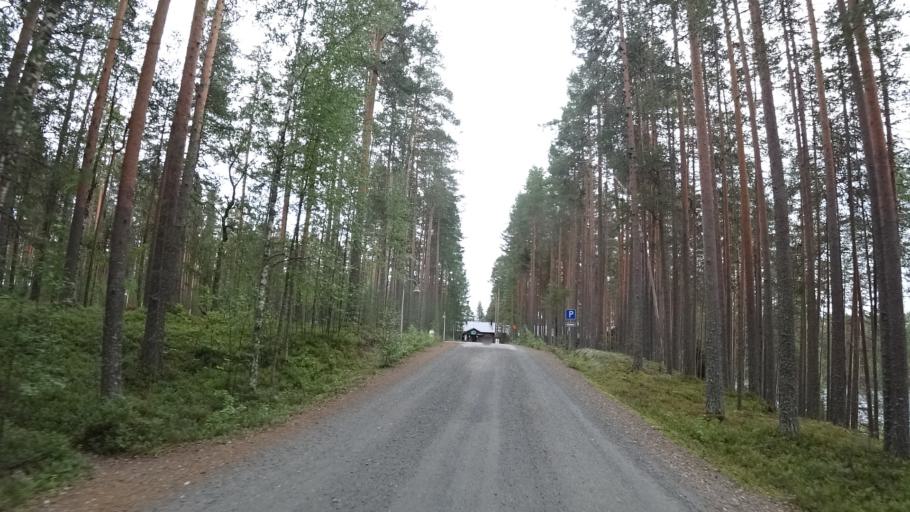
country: FI
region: North Karelia
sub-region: Joensuu
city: Ilomantsi
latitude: 62.5794
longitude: 31.1744
